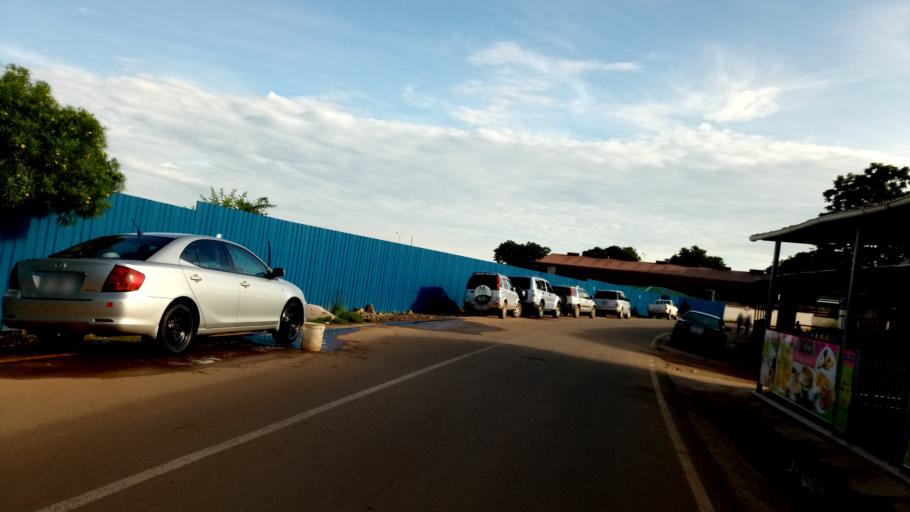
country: ZM
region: Lusaka
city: Lusaka
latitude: -15.4456
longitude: 28.3186
